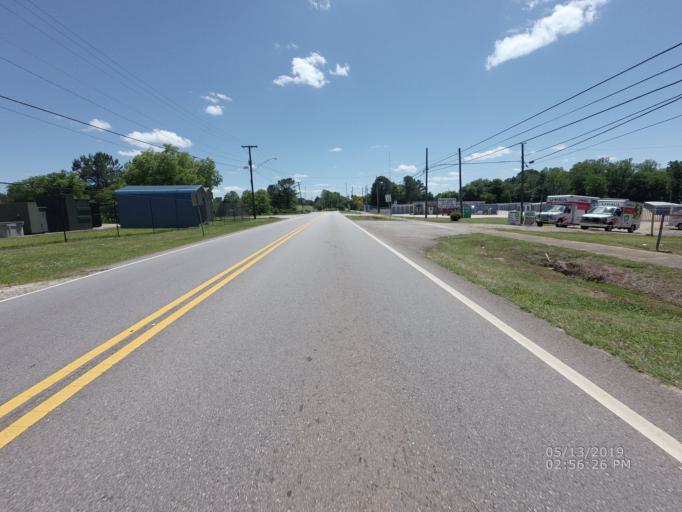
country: US
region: Georgia
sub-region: Troup County
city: West Point
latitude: 32.8828
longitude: -85.1712
